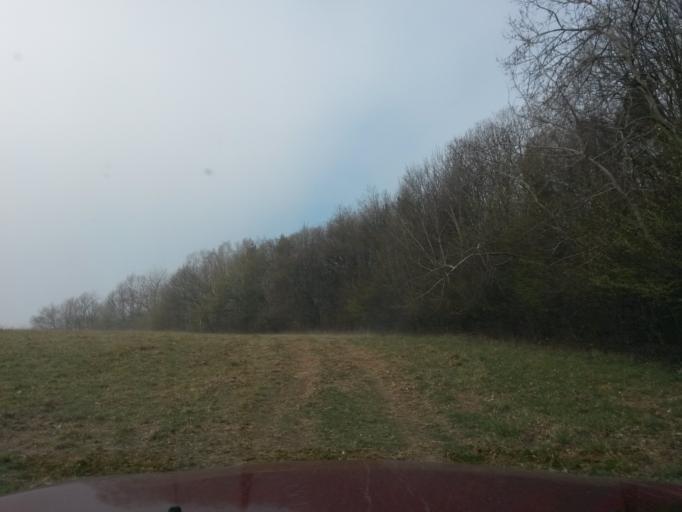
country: SK
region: Presovsky
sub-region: Okres Presov
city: Presov
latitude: 48.9218
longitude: 21.1746
